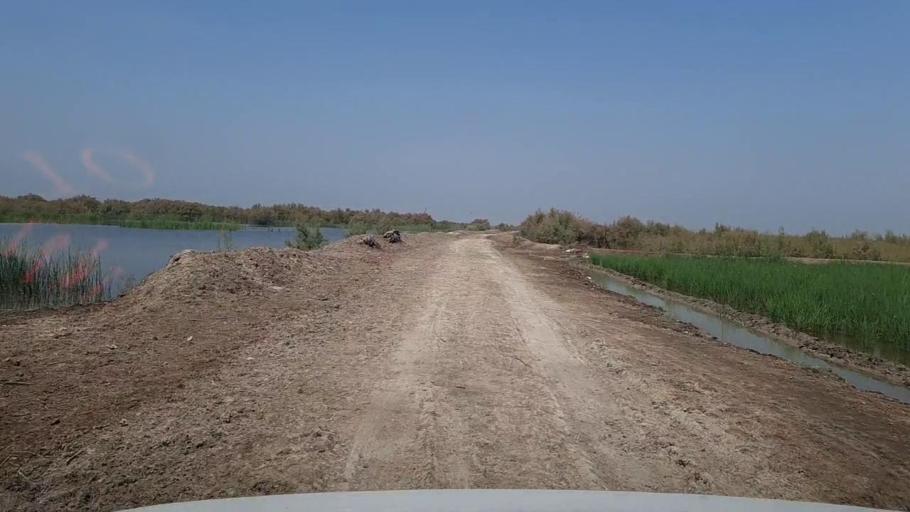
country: PK
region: Sindh
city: Kandhkot
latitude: 28.3429
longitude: 69.3021
